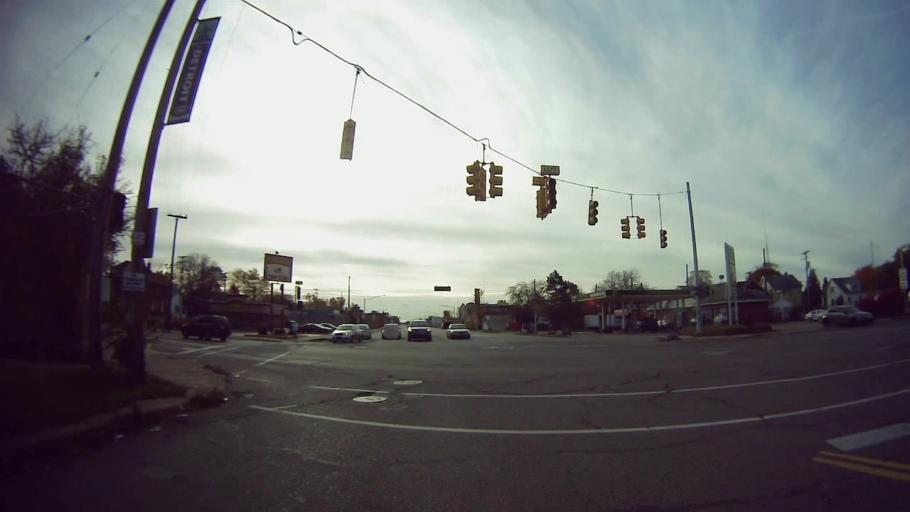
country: US
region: Michigan
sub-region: Wayne County
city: Highland Park
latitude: 42.4176
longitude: -83.1167
